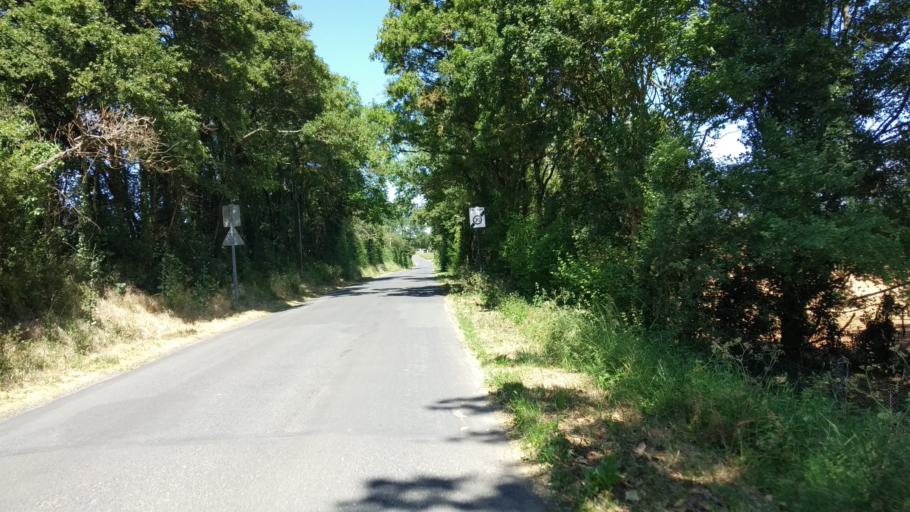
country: FR
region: Poitou-Charentes
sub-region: Departement de la Vienne
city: Vouneuil-sous-Biard
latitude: 46.6090
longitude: 0.2765
